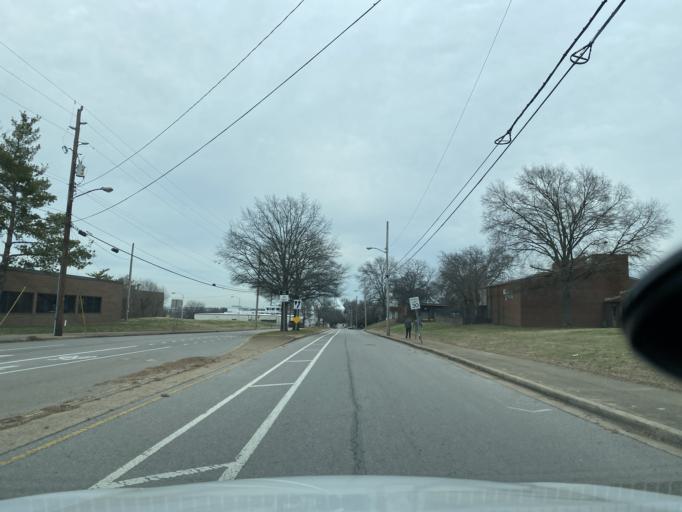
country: US
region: Tennessee
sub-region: Davidson County
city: Nashville
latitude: 36.1473
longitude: -86.7855
